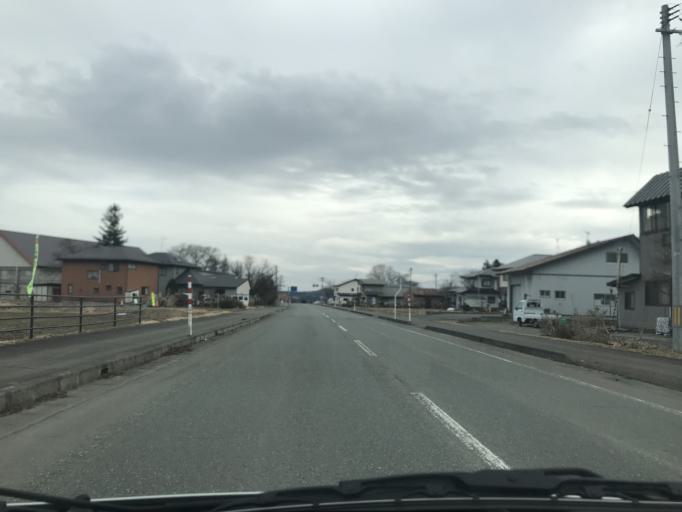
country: JP
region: Iwate
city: Kitakami
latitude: 39.3133
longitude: 140.9758
